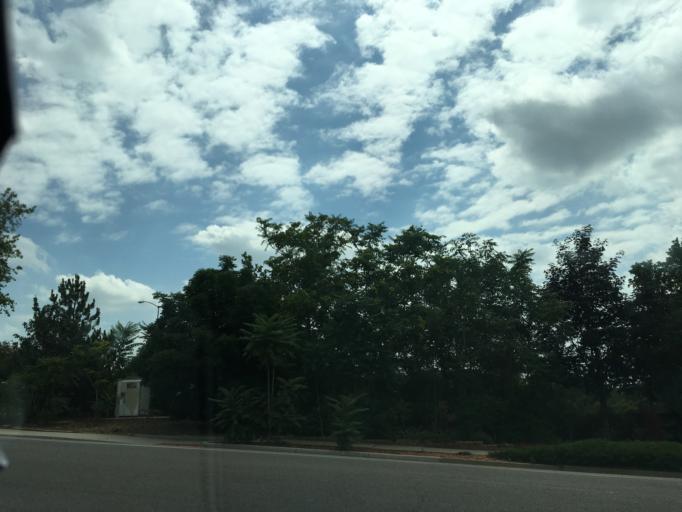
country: US
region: Colorado
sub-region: Arapahoe County
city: Sheridan
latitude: 39.6634
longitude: -105.0349
